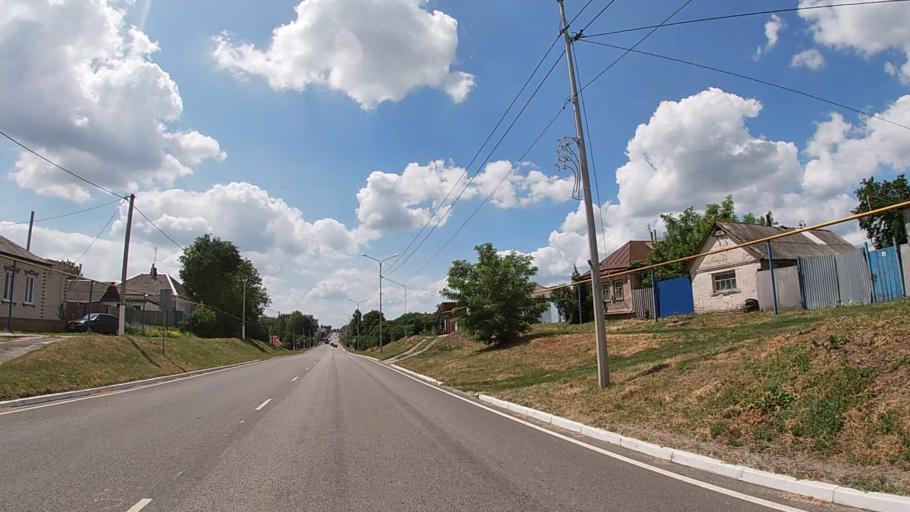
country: RU
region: Belgorod
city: Grayvoron
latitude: 50.4849
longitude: 35.6883
